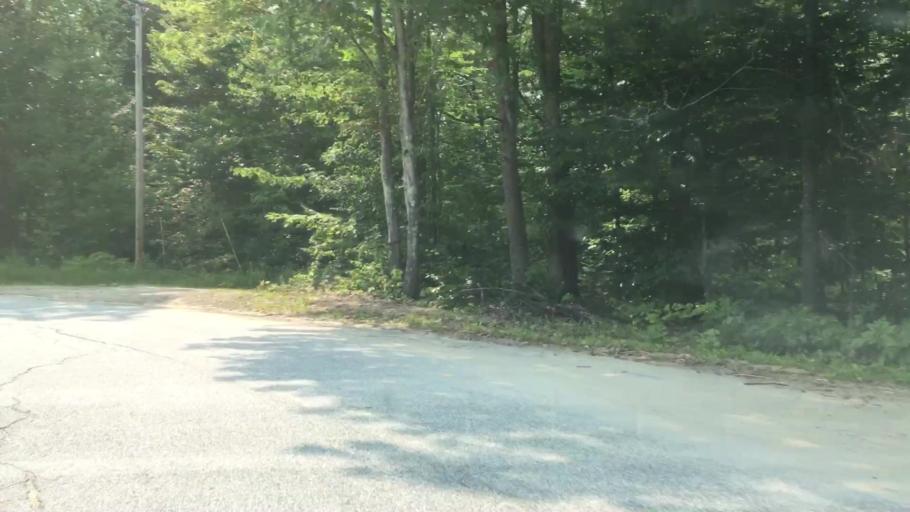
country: US
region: Maine
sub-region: Androscoggin County
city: Livermore
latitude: 44.3341
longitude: -70.2908
